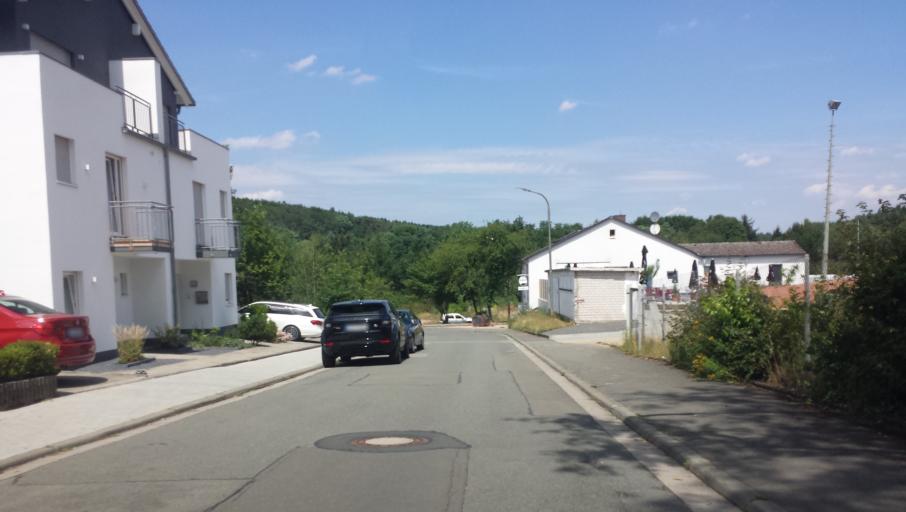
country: DE
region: Rheinland-Pfalz
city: Neuhemsbach
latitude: 49.4942
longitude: 7.9246
